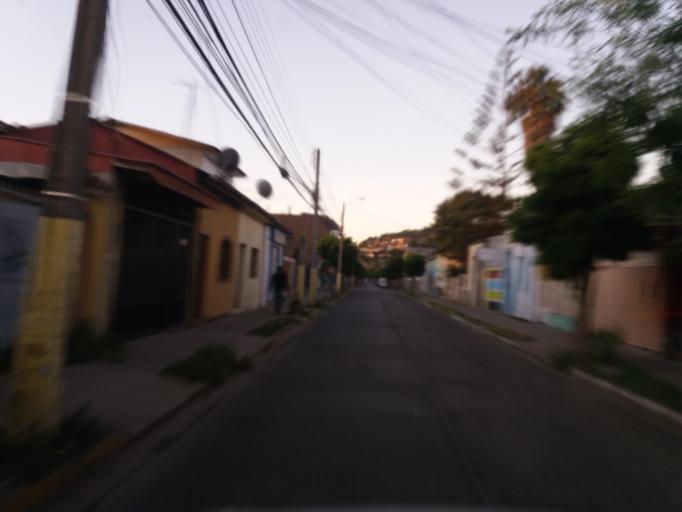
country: CL
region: Valparaiso
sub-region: Provincia de Quillota
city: Quillota
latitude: -32.8810
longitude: -71.2522
